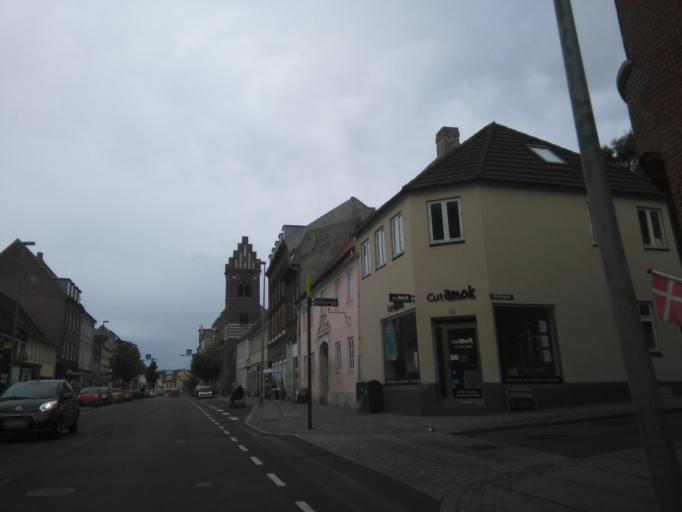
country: DK
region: Central Jutland
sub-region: Horsens Kommune
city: Horsens
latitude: 55.8626
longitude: 9.8514
